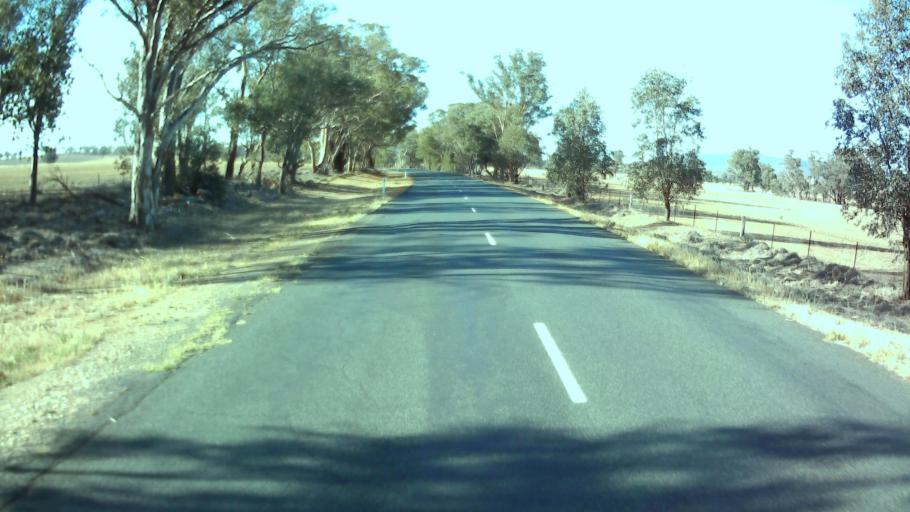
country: AU
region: New South Wales
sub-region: Weddin
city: Grenfell
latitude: -33.9286
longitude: 148.1377
